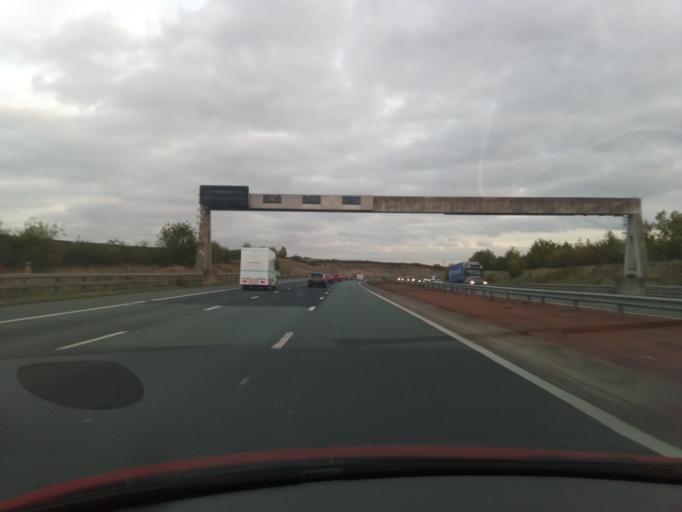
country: GB
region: England
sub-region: City and Borough of Leeds
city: Aberford
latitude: 53.7993
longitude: -1.3296
